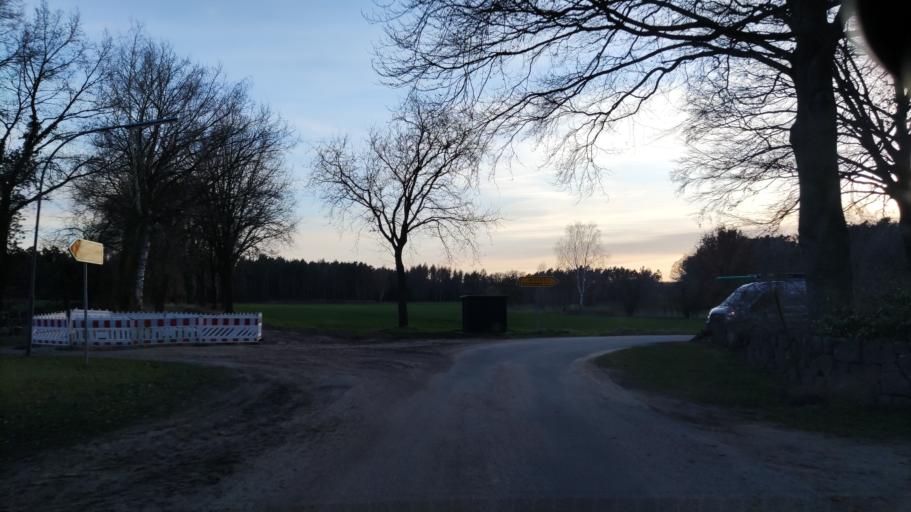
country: DE
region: Lower Saxony
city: Thomasburg
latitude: 53.2078
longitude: 10.6995
